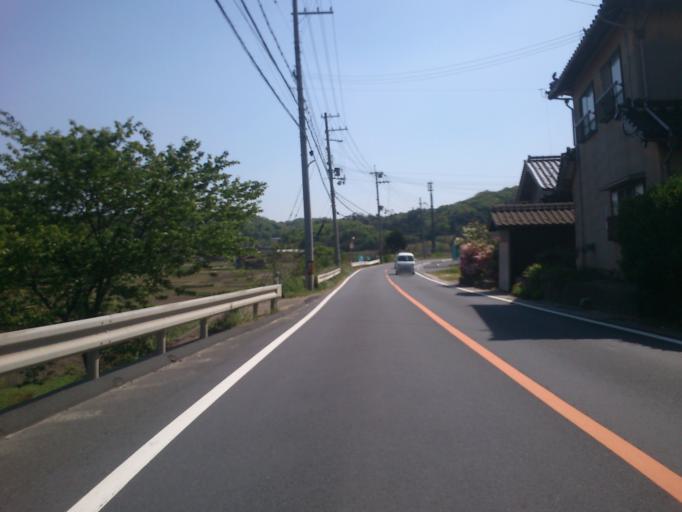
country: JP
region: Kyoto
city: Miyazu
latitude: 35.6976
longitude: 135.0556
